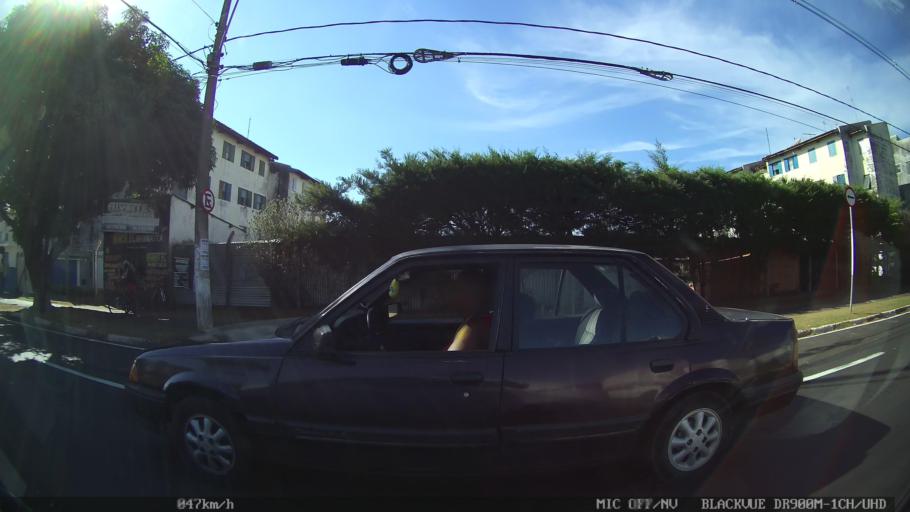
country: BR
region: Sao Paulo
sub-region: Franca
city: Franca
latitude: -20.5021
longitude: -47.4099
